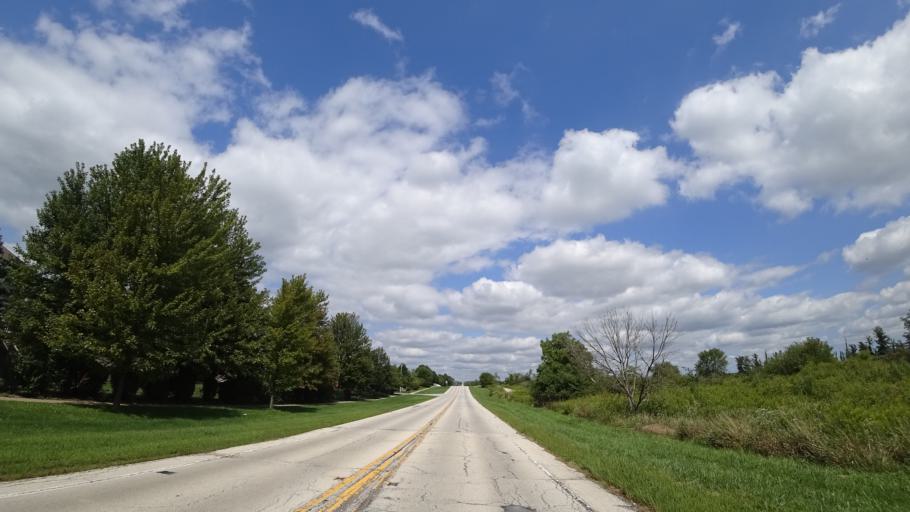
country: US
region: Illinois
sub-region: Cook County
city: Orland Hills
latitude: 41.5677
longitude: -87.8711
